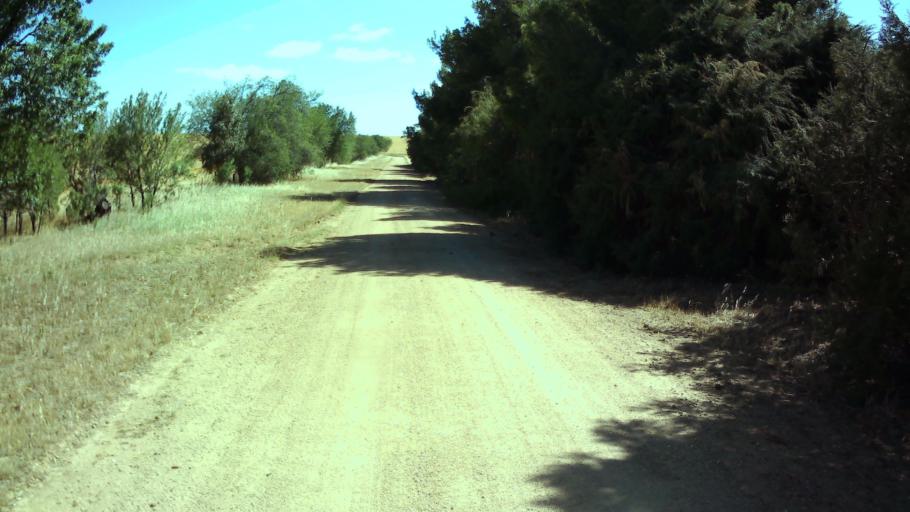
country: AU
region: New South Wales
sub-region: Weddin
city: Grenfell
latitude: -33.9679
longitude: 148.4106
